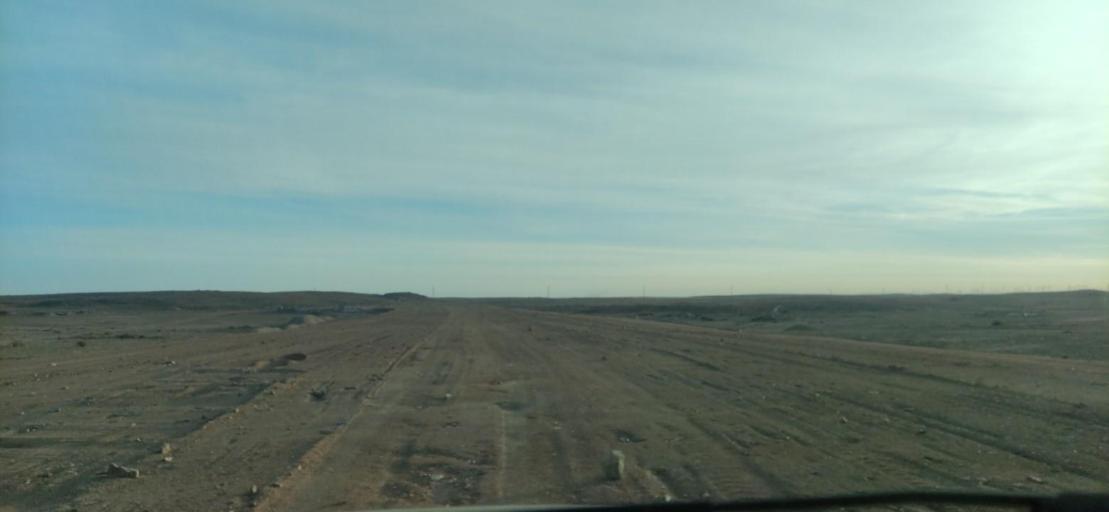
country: KZ
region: Qaraghandy
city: Saryshaghan
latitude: 46.1132
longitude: 73.5952
